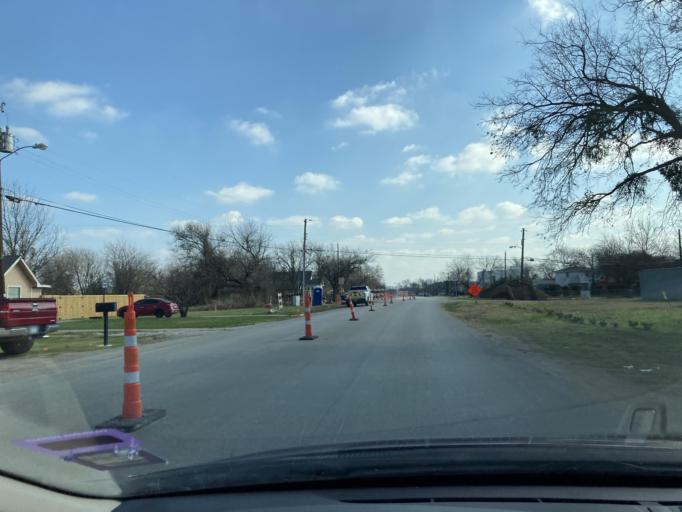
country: US
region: Texas
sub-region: Dallas County
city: Dallas
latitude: 32.7909
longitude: -96.8486
